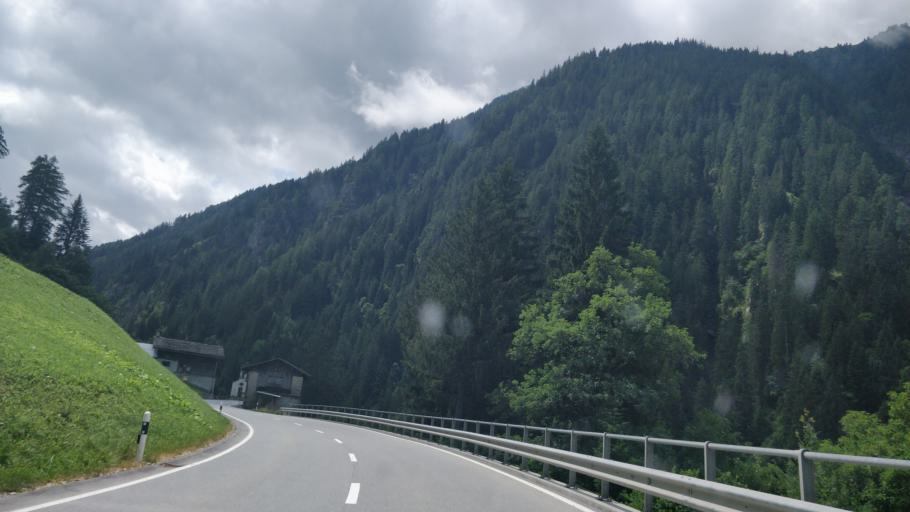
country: CH
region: Grisons
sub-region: Hinterrhein District
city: Hinterrhein
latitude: 46.6535
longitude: 9.1882
